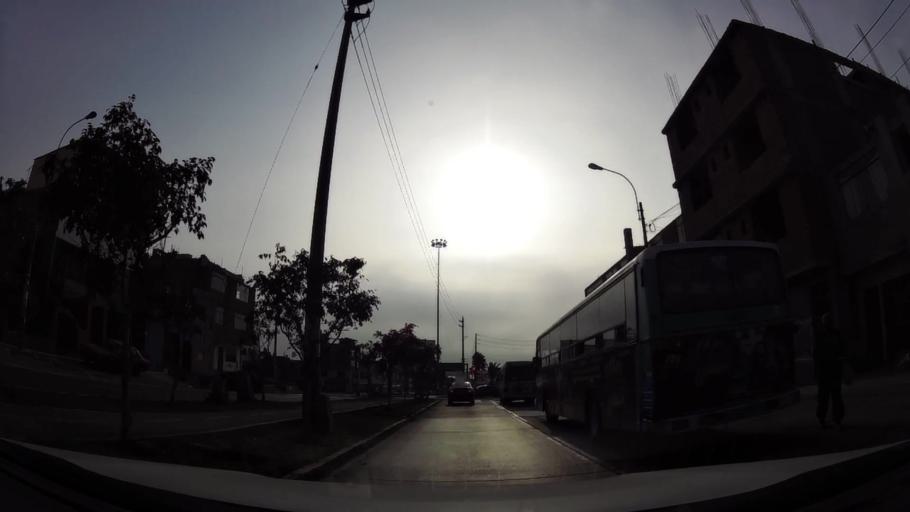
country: PE
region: Callao
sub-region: Callao
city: Callao
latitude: -12.0197
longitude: -77.0896
